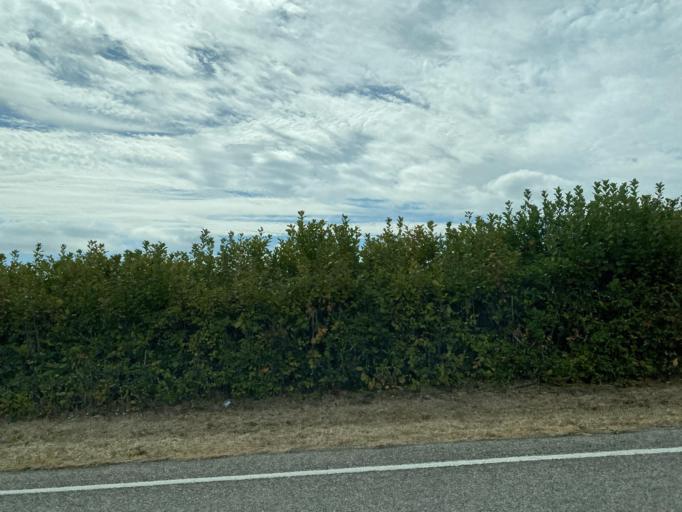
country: US
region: Washington
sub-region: Island County
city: Coupeville
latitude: 48.2370
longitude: -122.7160
